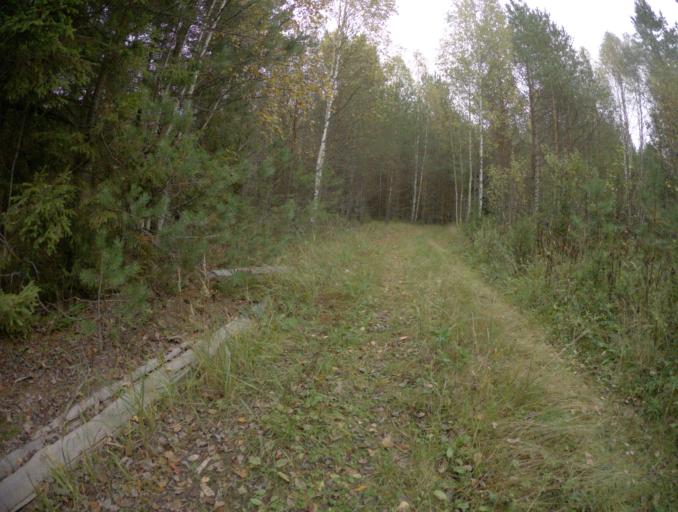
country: RU
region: Vladimir
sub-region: Kovrovskiy Rayon
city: Kovrov
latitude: 56.3346
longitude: 41.4595
